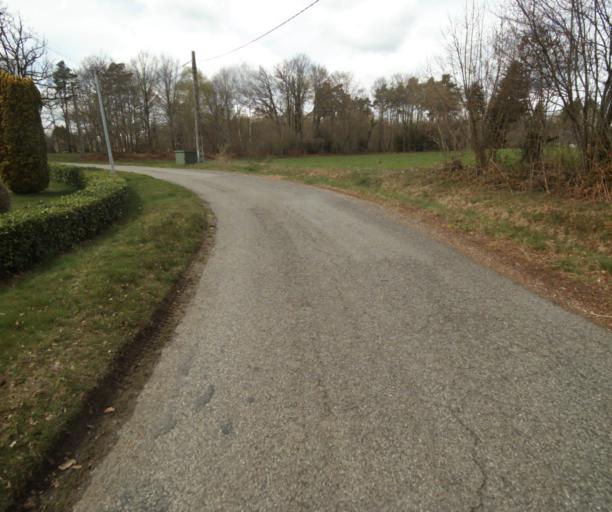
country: FR
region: Limousin
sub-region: Departement de la Correze
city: Laguenne
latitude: 45.2214
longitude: 1.8887
